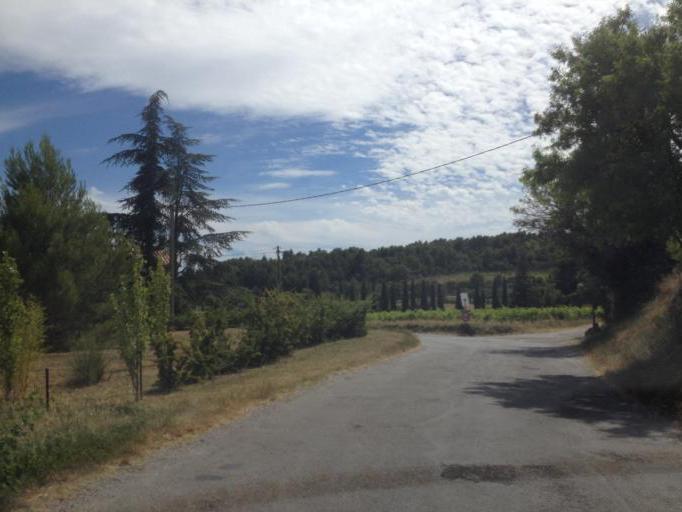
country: FR
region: Provence-Alpes-Cote d'Azur
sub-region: Departement du Vaucluse
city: Caromb
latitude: 44.1446
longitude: 5.0959
